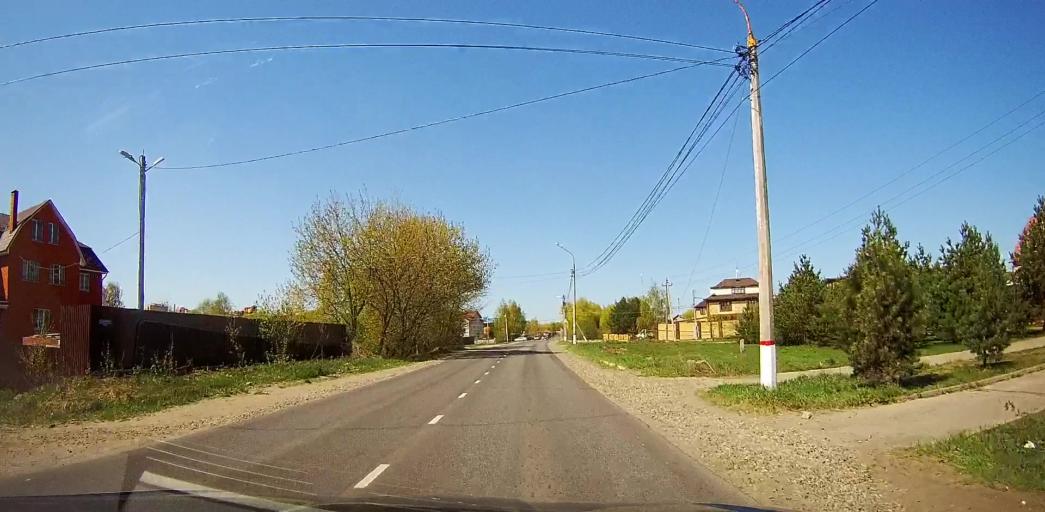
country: RU
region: Moskovskaya
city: Ramenskoye
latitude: 55.5825
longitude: 38.2615
